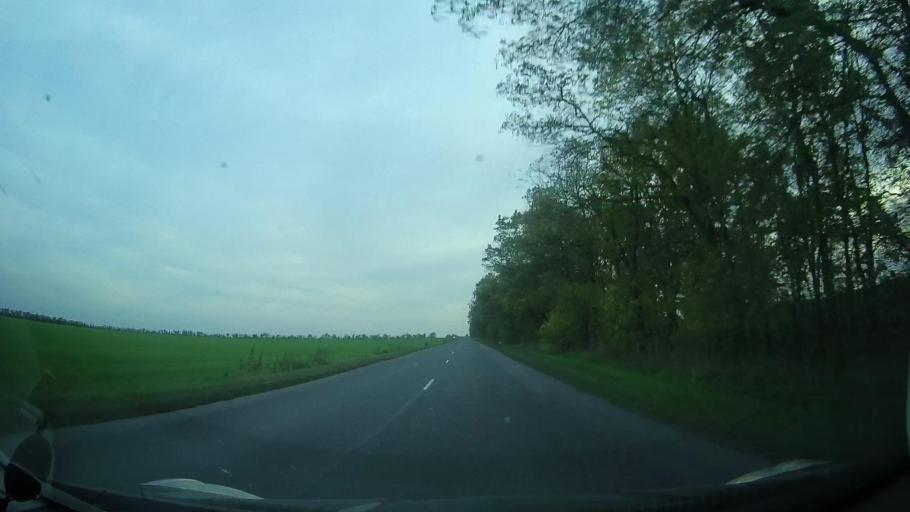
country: RU
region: Rostov
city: Kirovskaya
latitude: 47.0466
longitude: 39.9769
